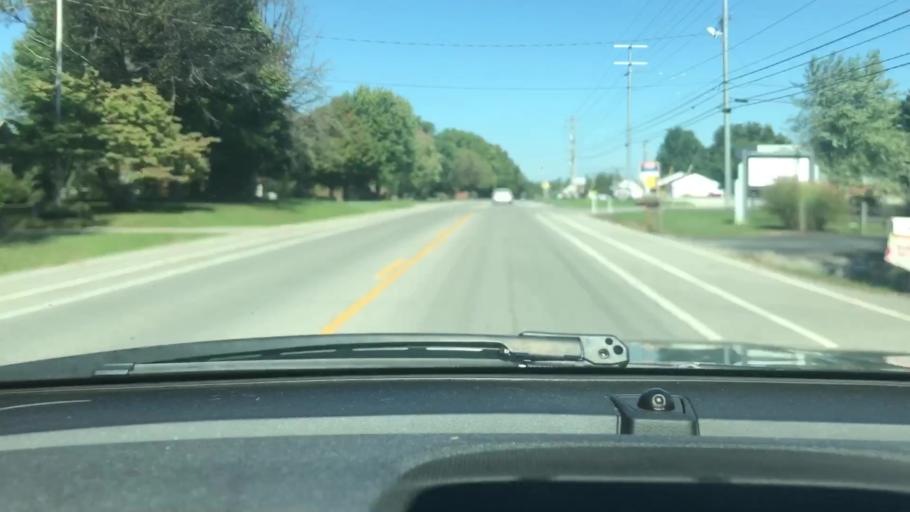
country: US
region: Tennessee
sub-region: Sumner County
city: White House
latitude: 36.4464
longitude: -86.6774
